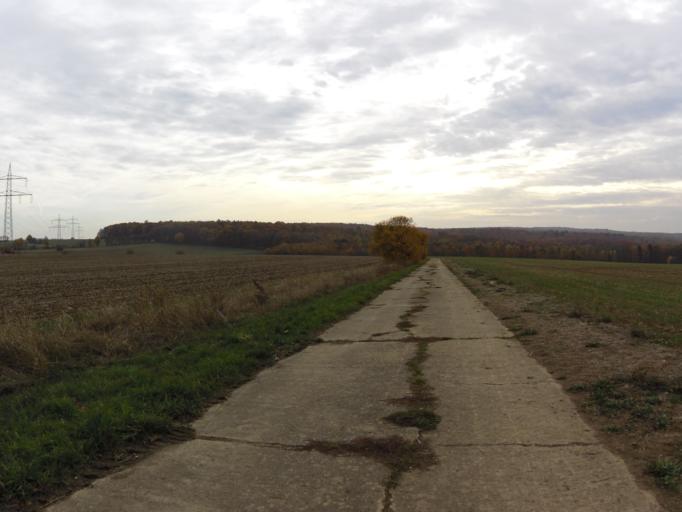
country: DE
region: Bavaria
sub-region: Regierungsbezirk Unterfranken
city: Kist
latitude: 49.7418
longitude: 9.8331
